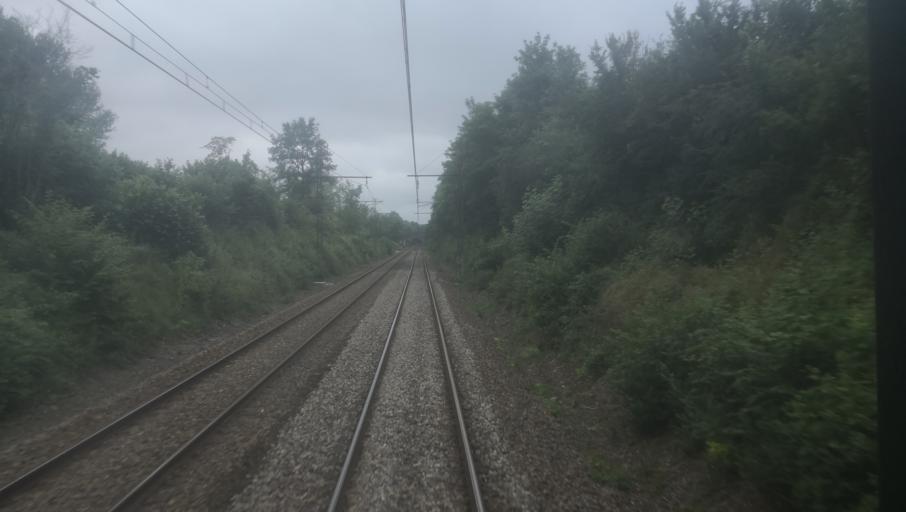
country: FR
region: Centre
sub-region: Departement de l'Indre
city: Reuilly
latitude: 47.0592
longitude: 2.0395
